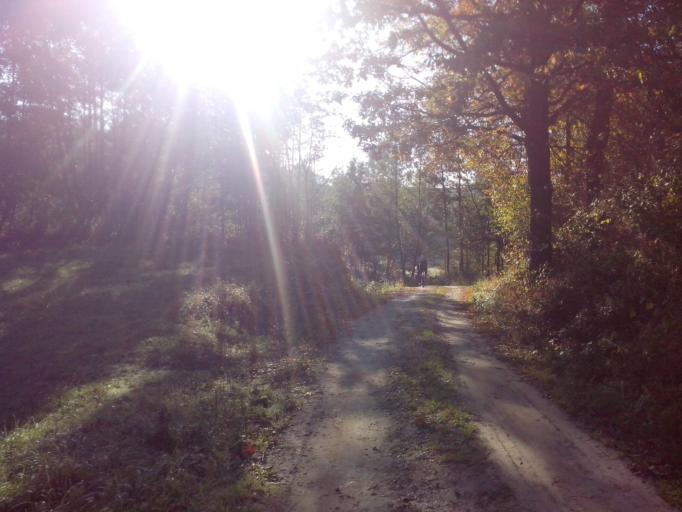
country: PL
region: Kujawsko-Pomorskie
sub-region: Powiat brodnicki
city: Gorzno
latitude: 53.2139
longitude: 19.6534
